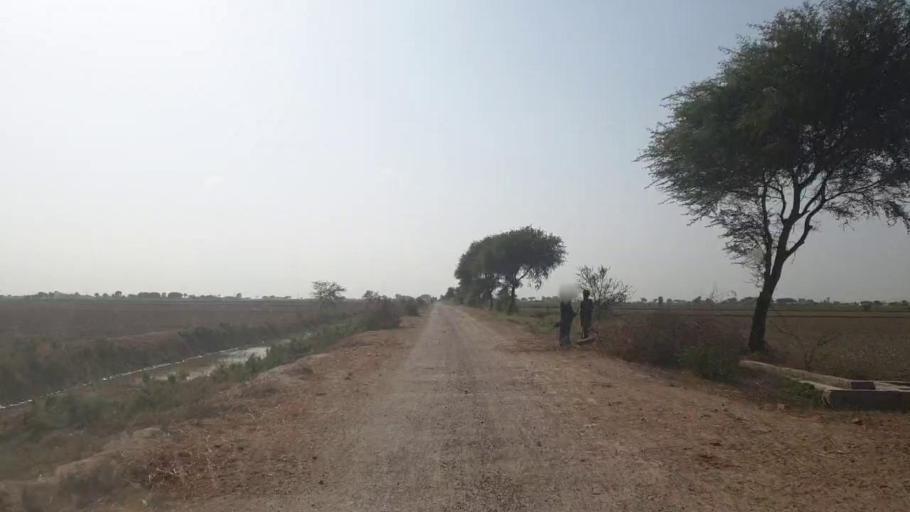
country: PK
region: Sindh
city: Kario
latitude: 24.5589
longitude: 68.5125
